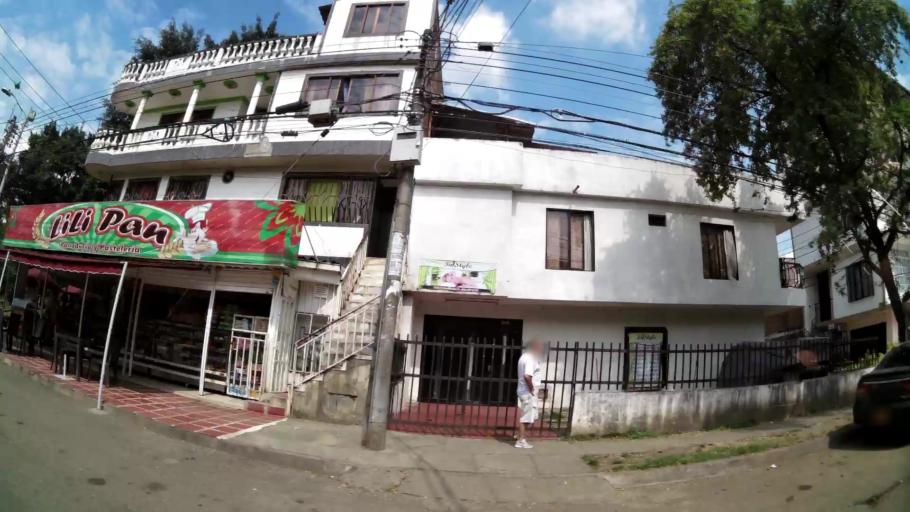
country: CO
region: Valle del Cauca
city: Cali
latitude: 3.4865
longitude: -76.4975
